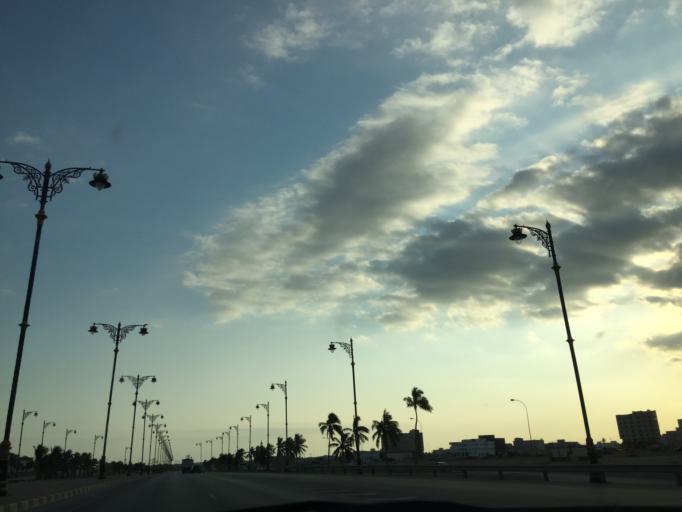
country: OM
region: Zufar
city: Salalah
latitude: 17.0295
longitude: 54.0589
